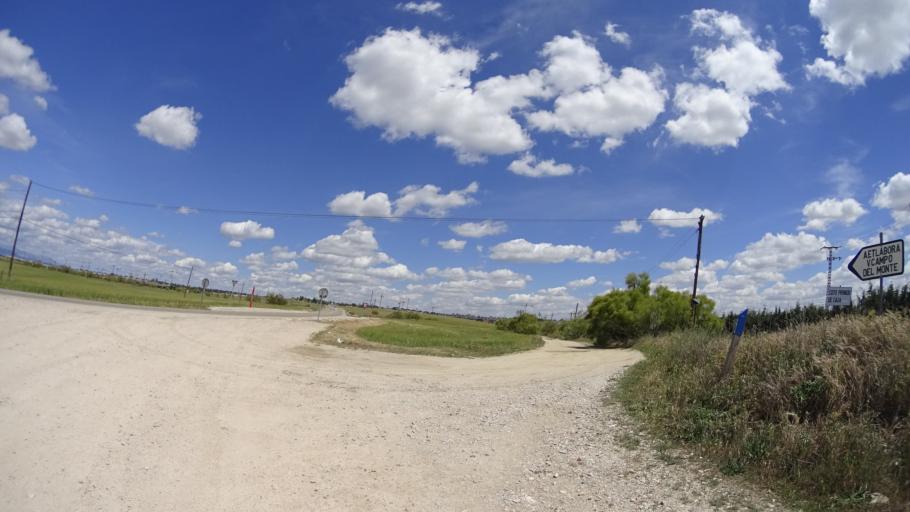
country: ES
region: Madrid
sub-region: Provincia de Madrid
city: Boadilla del Monte
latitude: 40.4119
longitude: -3.9253
